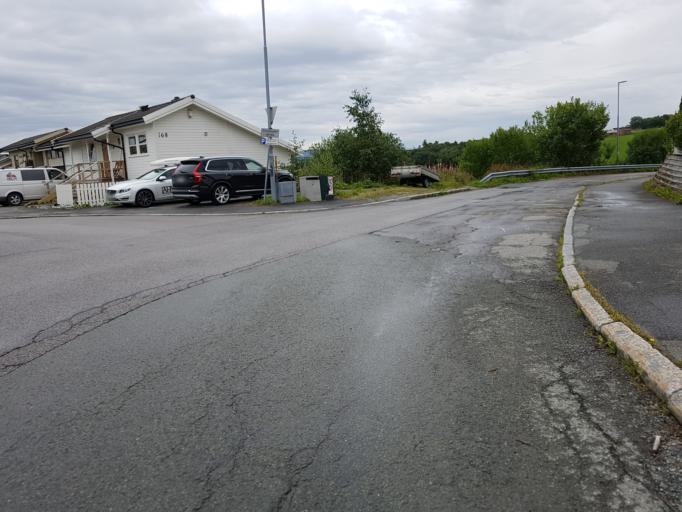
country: NO
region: Sor-Trondelag
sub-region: Trondheim
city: Trondheim
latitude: 63.3852
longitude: 10.3432
